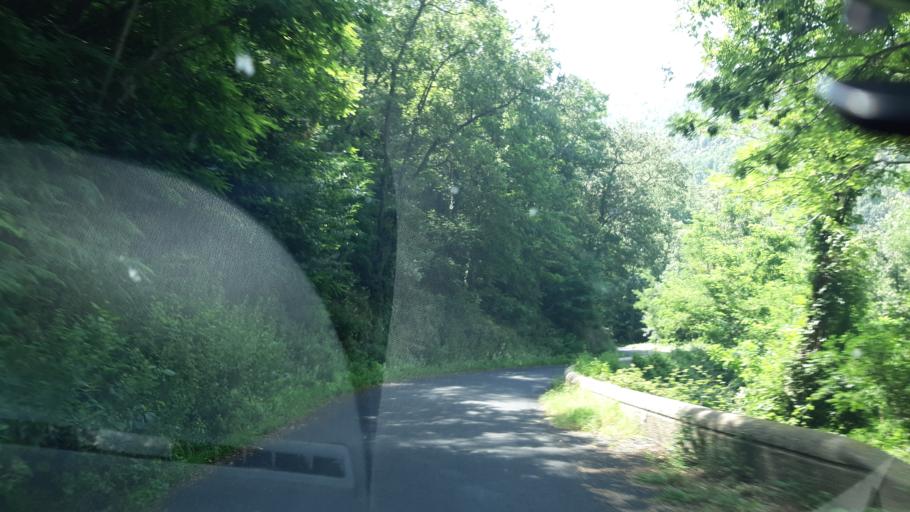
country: FR
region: Languedoc-Roussillon
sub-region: Departement des Pyrenees-Orientales
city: Arles
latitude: 42.5234
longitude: 2.6190
